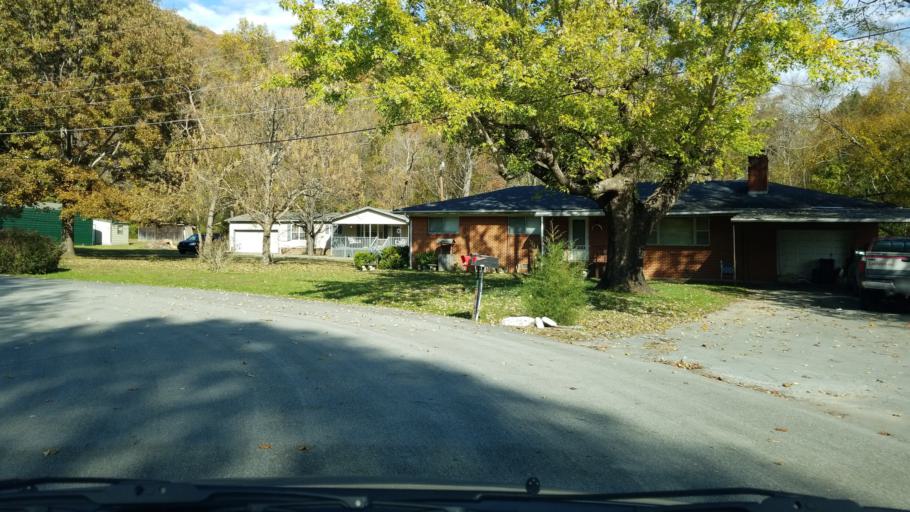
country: US
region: Tennessee
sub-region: Hamilton County
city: Soddy-Daisy
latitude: 35.2294
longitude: -85.2263
